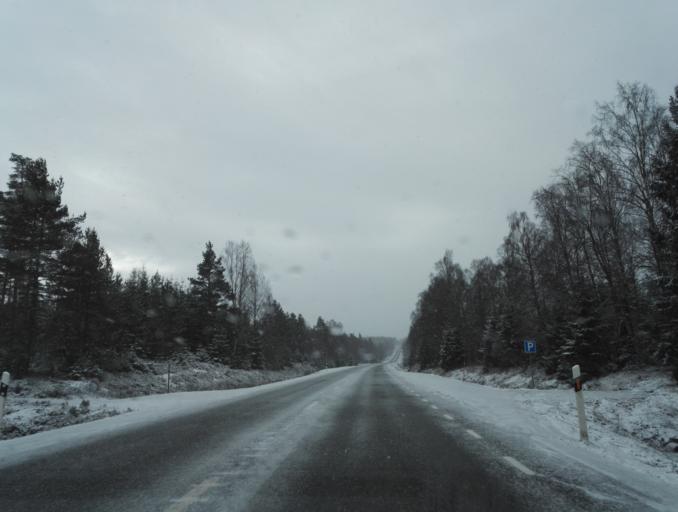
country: SE
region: Kronoberg
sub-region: Uppvidinge Kommun
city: Lenhovda
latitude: 57.0764
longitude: 15.1930
